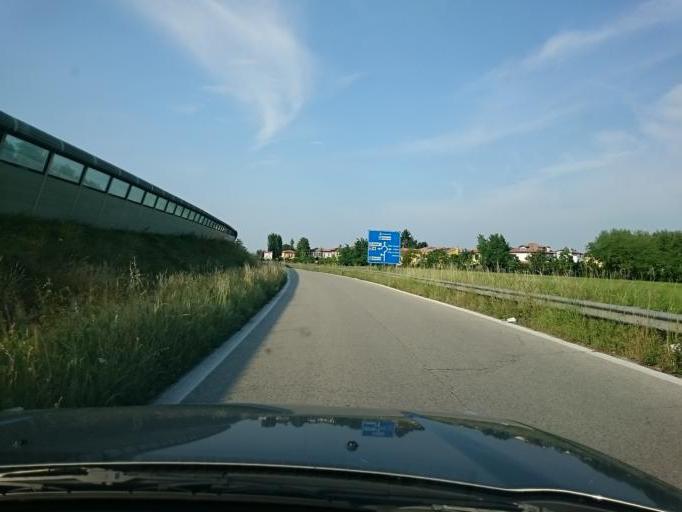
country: IT
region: Veneto
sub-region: Provincia di Padova
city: Ponte San Nicolo
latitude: 45.3731
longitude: 11.9073
